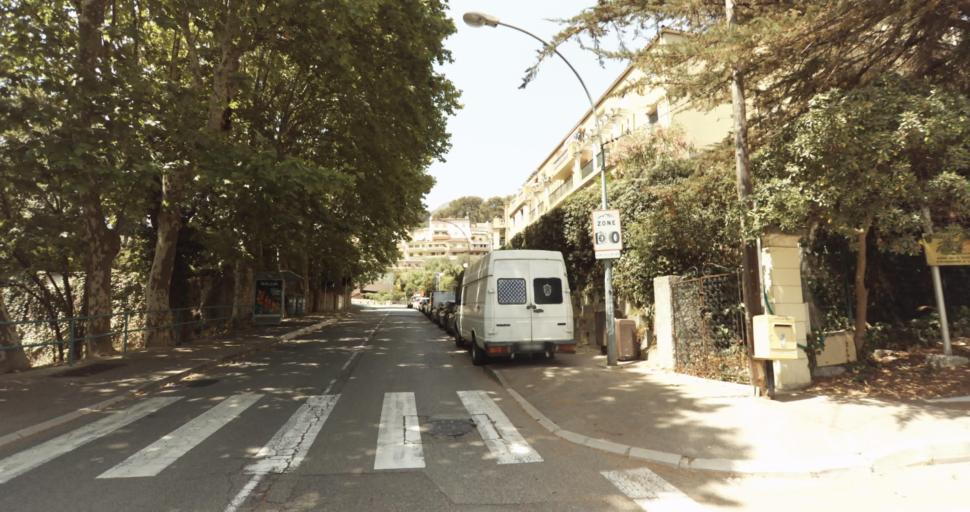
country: FR
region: Provence-Alpes-Cote d'Azur
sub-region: Departement des Alpes-Maritimes
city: Roquebrune-Cap-Martin
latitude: 43.7777
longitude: 7.4719
